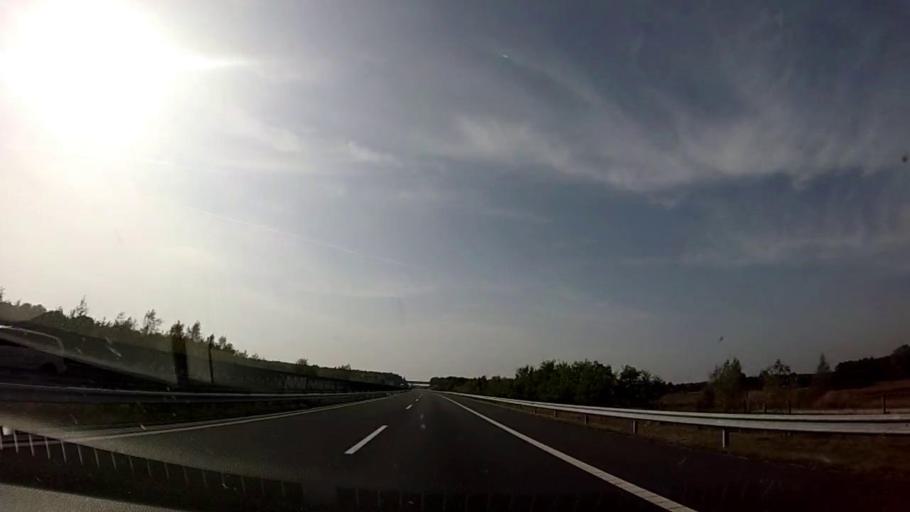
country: HU
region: Somogy
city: Balatonbereny
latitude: 46.6397
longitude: 17.2857
